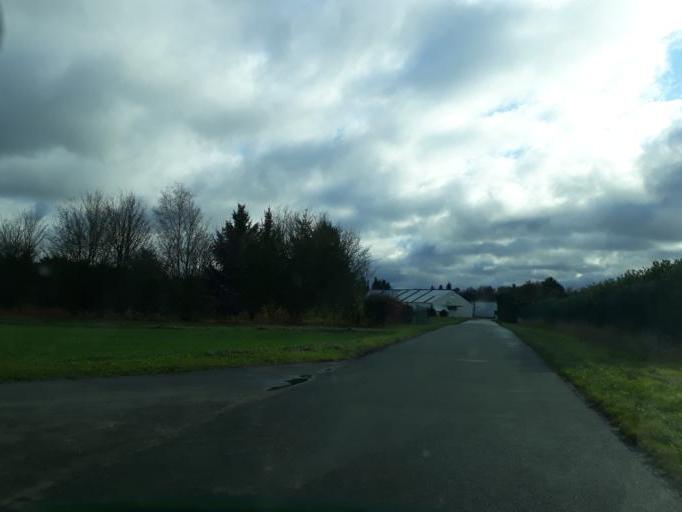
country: FR
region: Centre
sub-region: Departement du Loir-et-Cher
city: Mer
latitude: 47.7944
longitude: 1.5227
